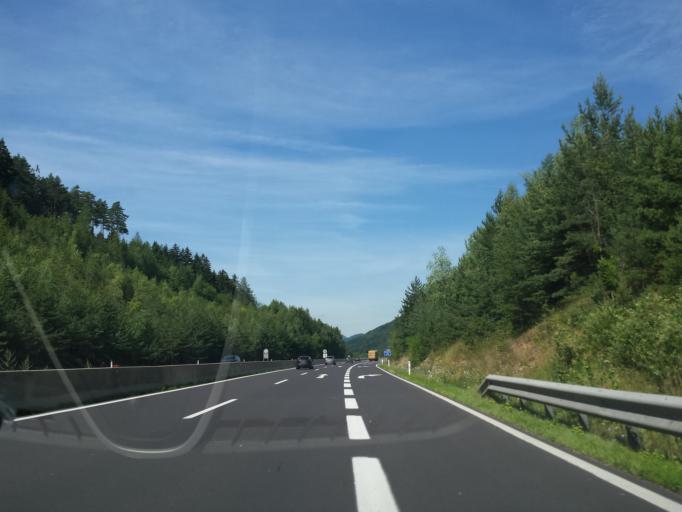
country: AT
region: Lower Austria
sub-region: Politischer Bezirk Neunkirchen
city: Enzenreith
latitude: 47.6622
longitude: 15.9451
